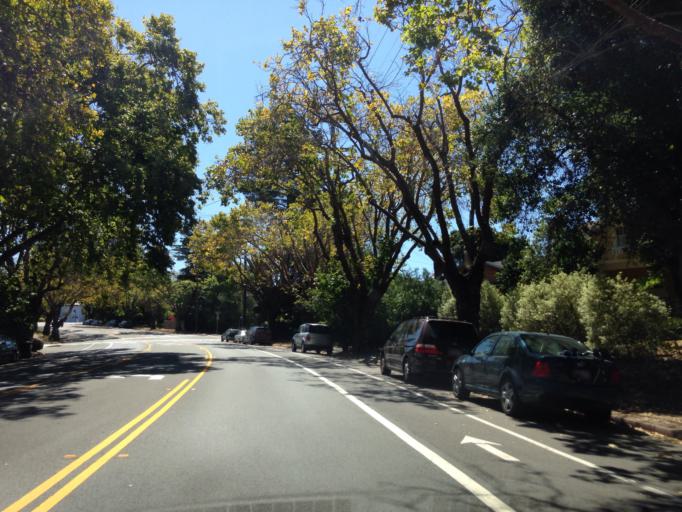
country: US
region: California
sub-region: Alameda County
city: Berkeley
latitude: 37.8893
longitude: -122.2786
